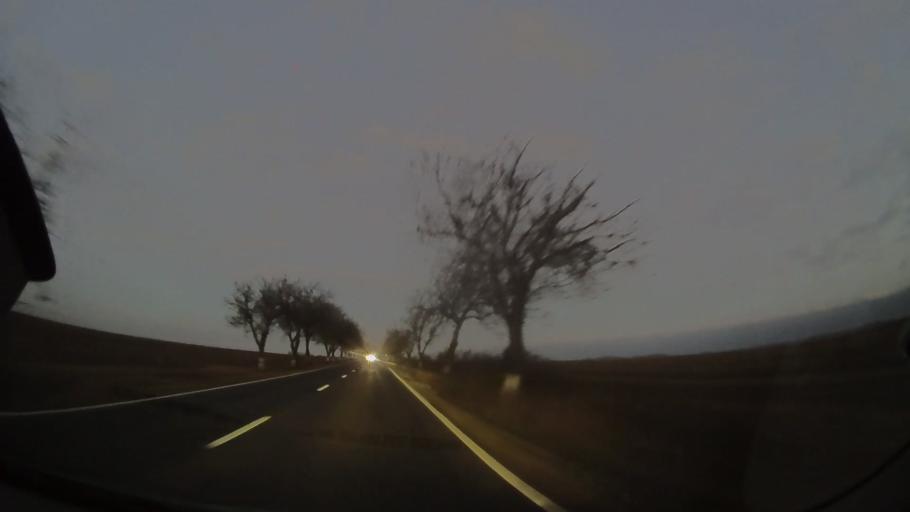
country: RO
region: Tulcea
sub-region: Comuna Frecatei
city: Cataloi
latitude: 45.0825
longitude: 28.6979
